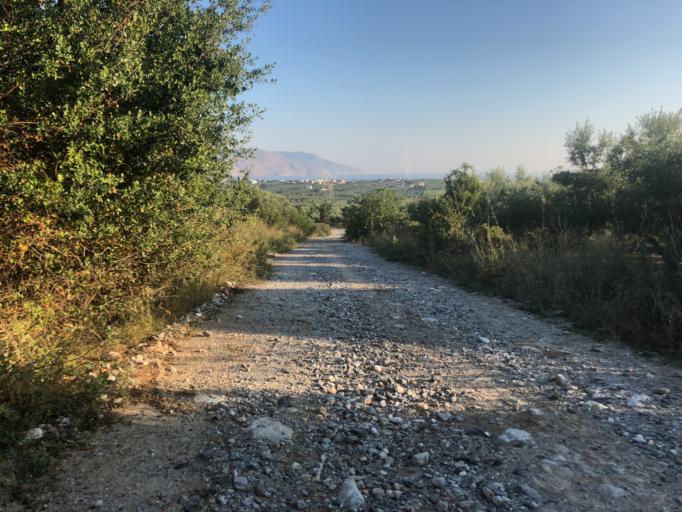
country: GR
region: Crete
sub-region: Nomos Chanias
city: Georgioupolis
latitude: 35.3370
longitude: 24.2902
